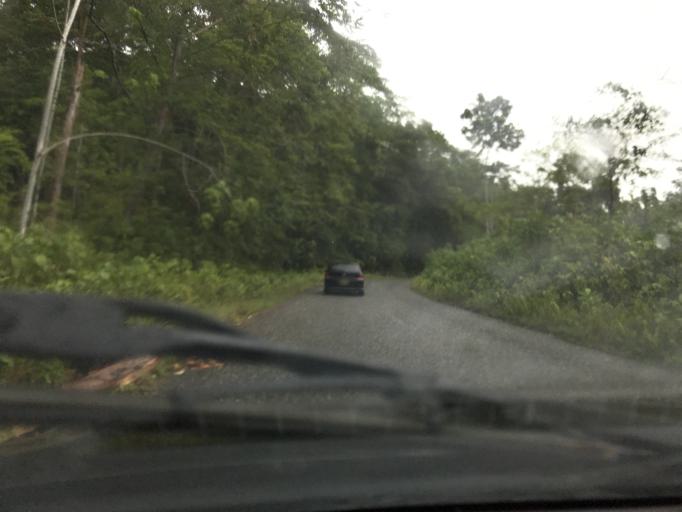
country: SB
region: Western Province
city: Gizo
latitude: -8.3000
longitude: 157.2522
